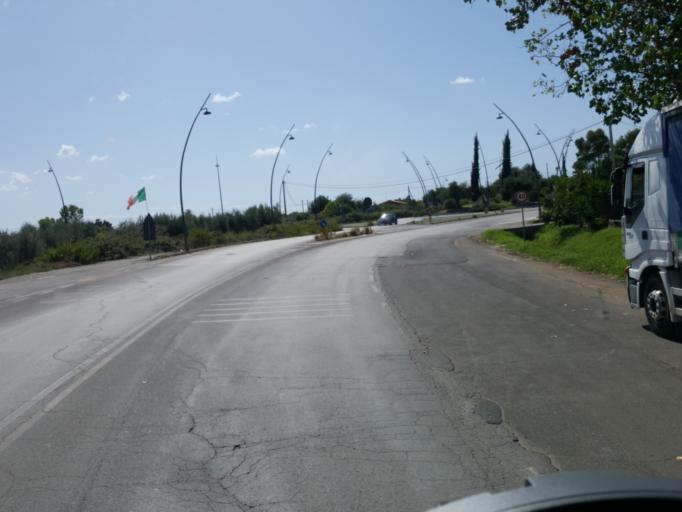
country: IT
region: Latium
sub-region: Provincia di Latina
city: Priverno
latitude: 41.4231
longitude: 13.1813
